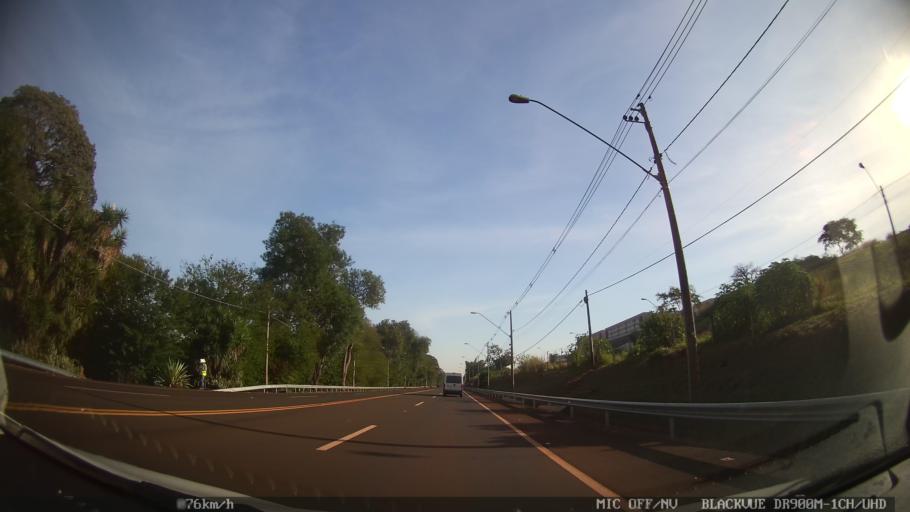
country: BR
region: Sao Paulo
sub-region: Cravinhos
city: Cravinhos
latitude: -21.2816
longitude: -47.8145
